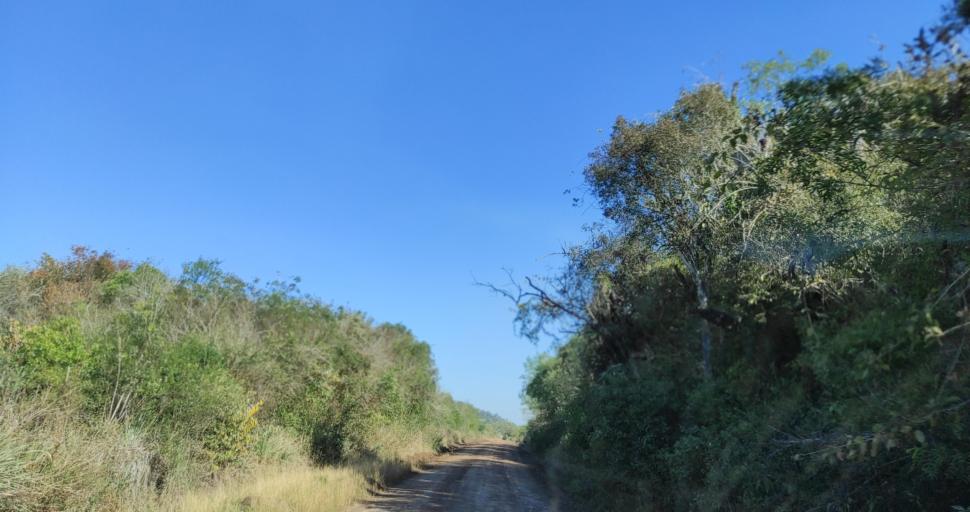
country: AR
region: Misiones
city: Cerro Cora
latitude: -27.6559
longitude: -55.6585
